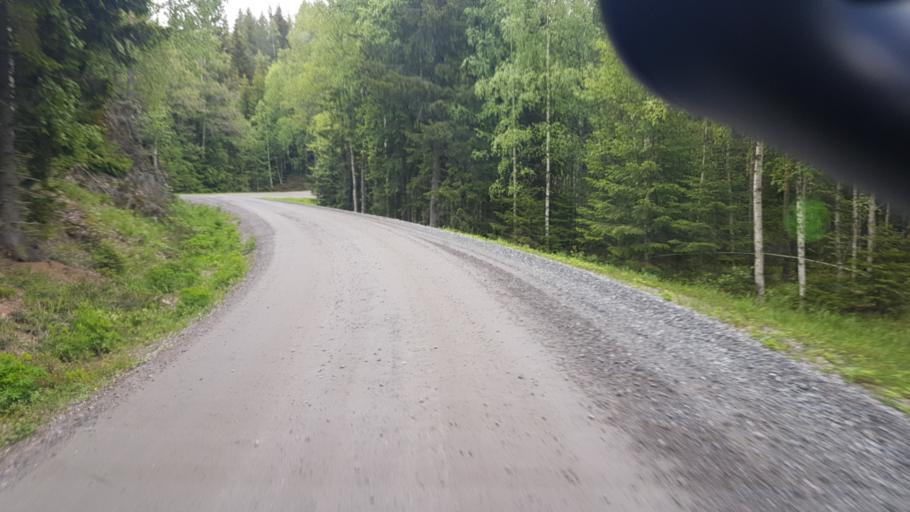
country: NO
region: Ostfold
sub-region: Romskog
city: Romskog
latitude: 59.7167
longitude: 11.9943
